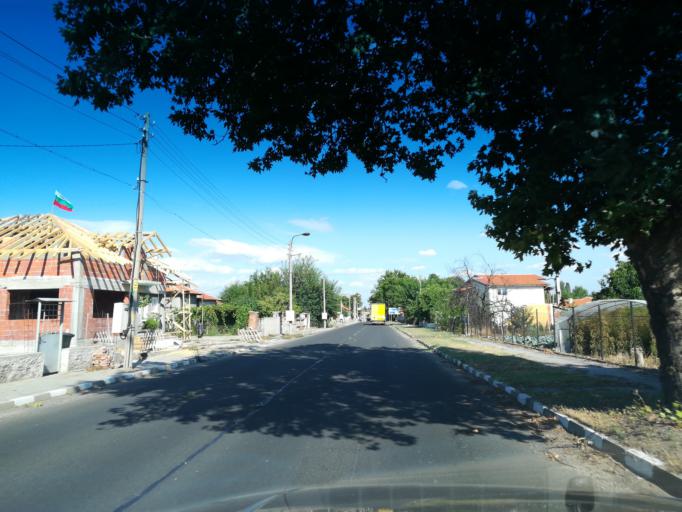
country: BG
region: Stara Zagora
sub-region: Obshtina Chirpan
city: Chirpan
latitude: 42.0586
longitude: 25.2592
